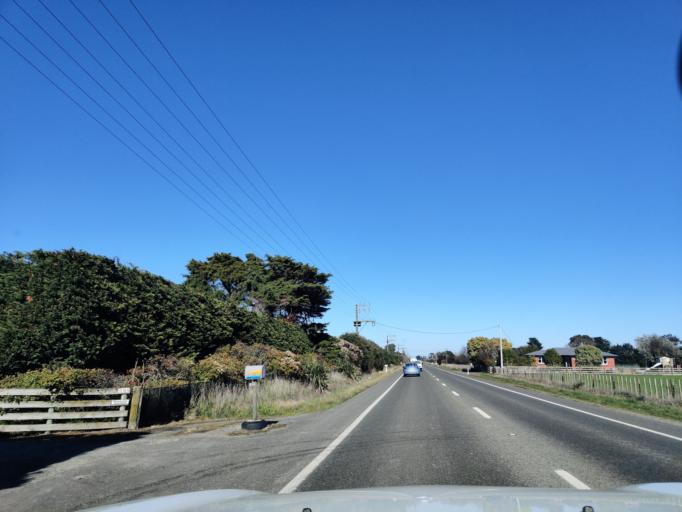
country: NZ
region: Manawatu-Wanganui
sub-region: Palmerston North City
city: Palmerston North
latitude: -40.2568
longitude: 175.5751
